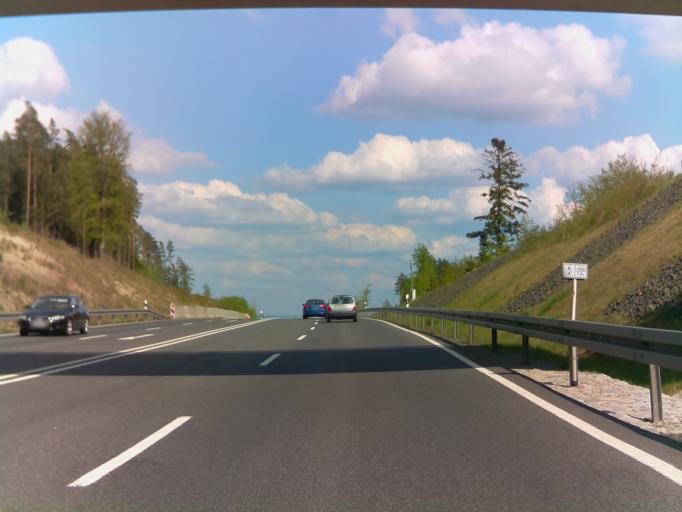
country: DE
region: Bavaria
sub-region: Upper Franconia
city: Rodental
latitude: 50.3055
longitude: 11.0441
